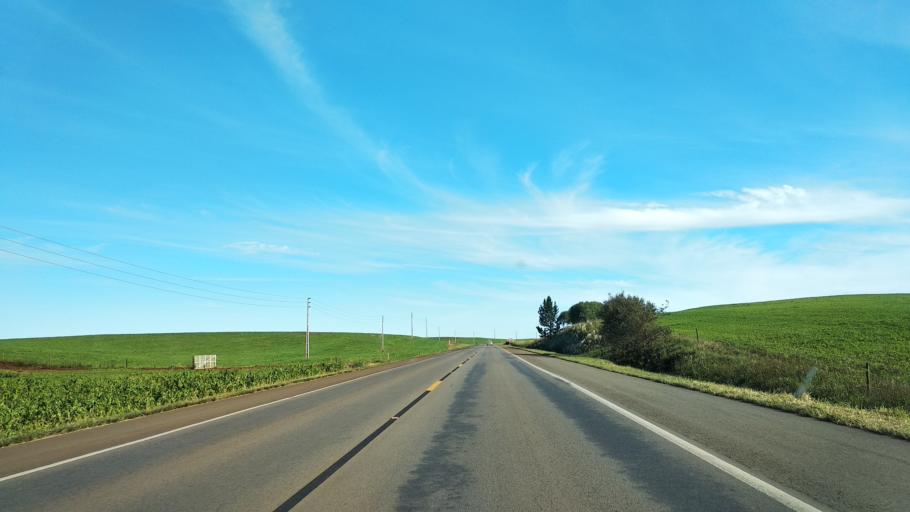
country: BR
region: Santa Catarina
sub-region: Celso Ramos
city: Celso Ramos
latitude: -27.5177
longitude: -51.3505
